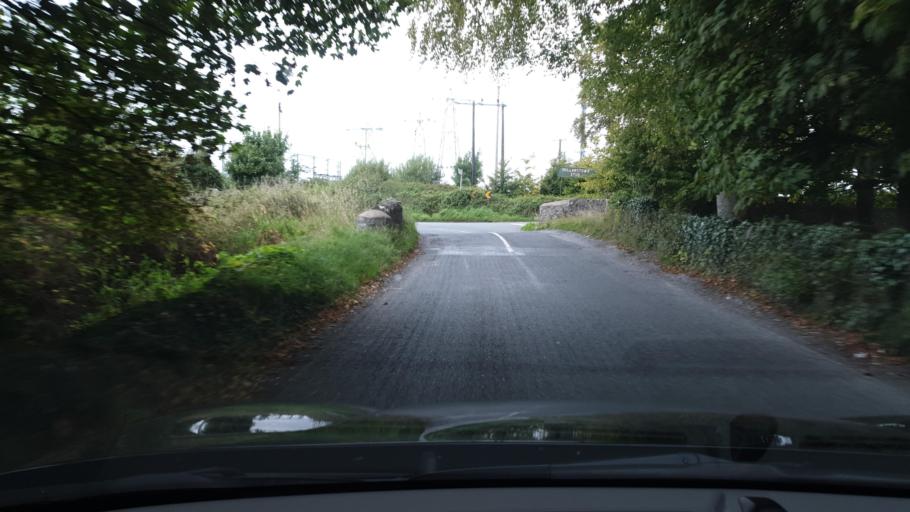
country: IE
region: Leinster
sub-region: Kildare
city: Kilcock
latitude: 53.4034
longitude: -6.6537
